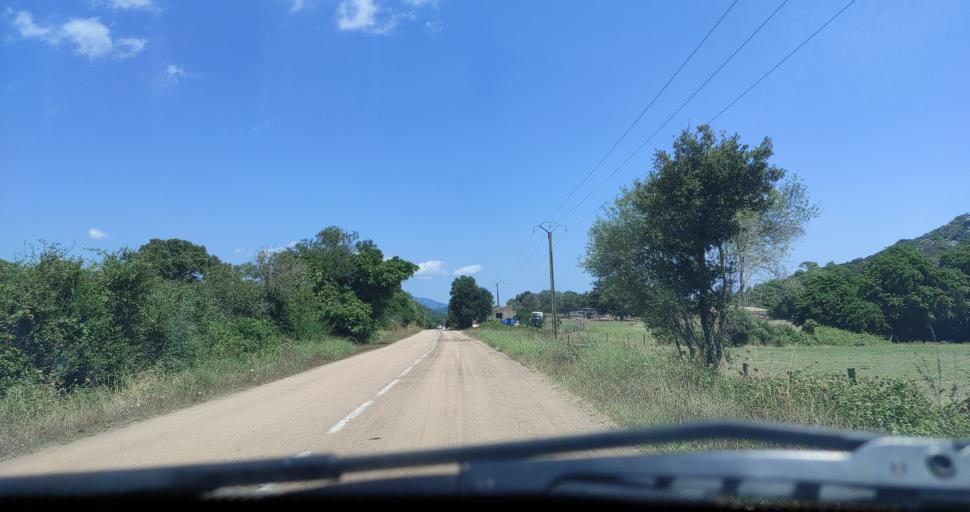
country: FR
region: Corsica
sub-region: Departement de la Corse-du-Sud
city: Porto-Vecchio
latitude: 41.5414
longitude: 9.1780
